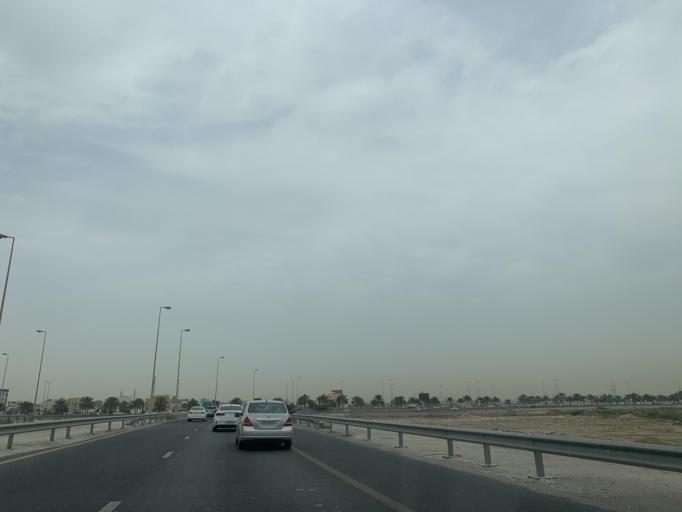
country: BH
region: Northern
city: Madinat `Isa
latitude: 26.1902
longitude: 50.5182
